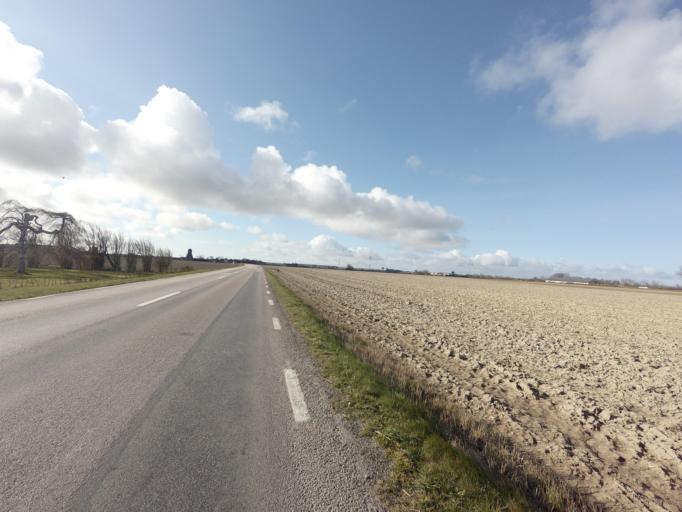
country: SE
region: Skane
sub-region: Helsingborg
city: Odakra
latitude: 56.1679
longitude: 12.6781
